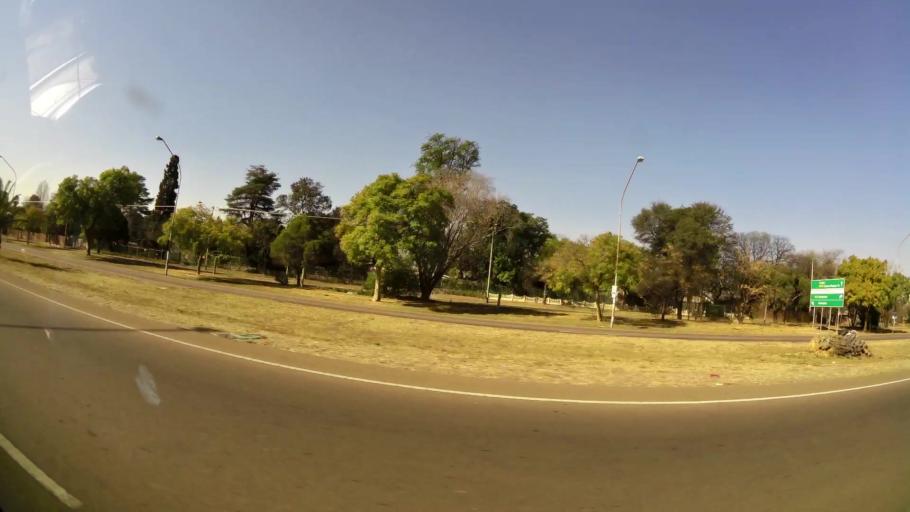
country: ZA
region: Gauteng
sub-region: City of Tshwane Metropolitan Municipality
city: Pretoria
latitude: -25.7310
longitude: 28.2586
